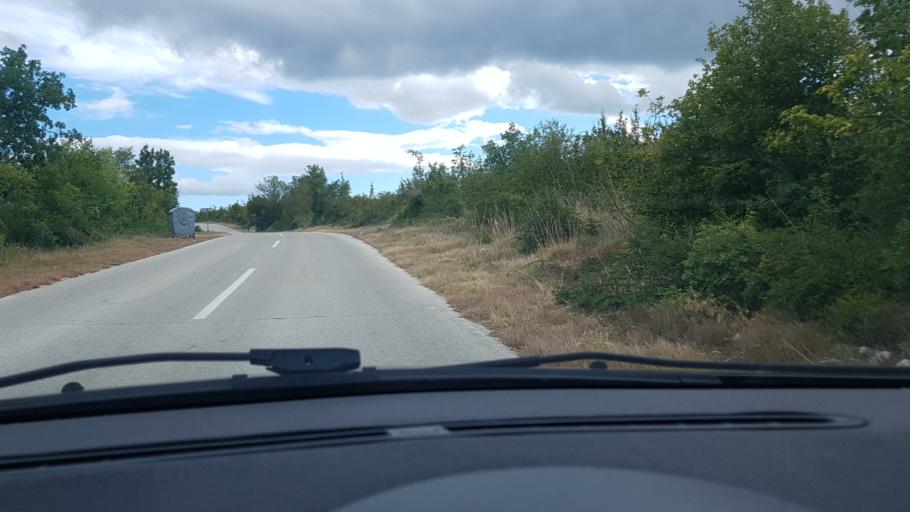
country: HR
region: Sibensko-Kniniska
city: Kistanje
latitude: 44.0963
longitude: 15.9365
